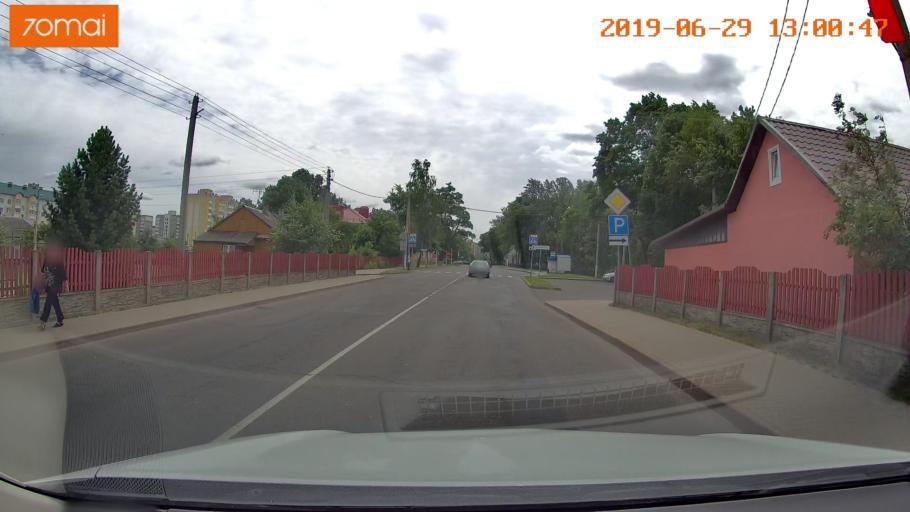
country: BY
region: Minsk
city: Slutsk
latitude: 53.0427
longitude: 27.5581
